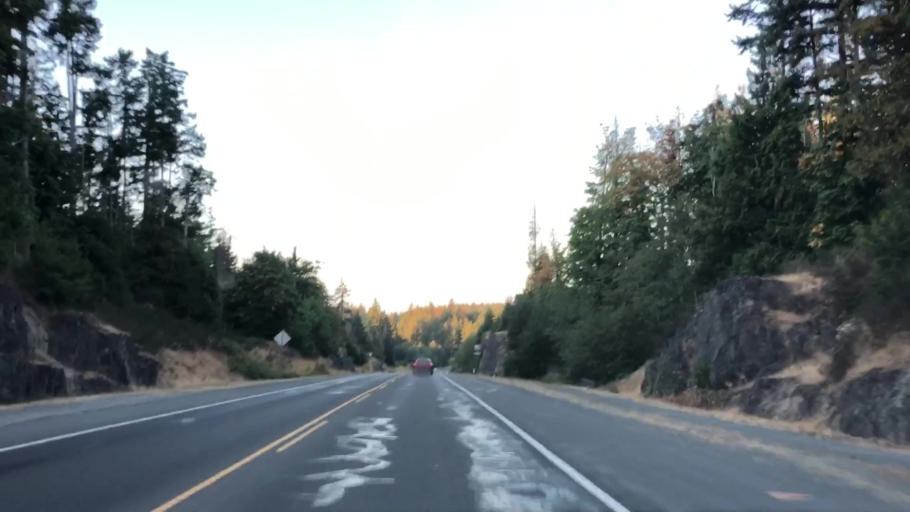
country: CA
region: British Columbia
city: Colwood
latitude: 48.4131
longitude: -123.5055
